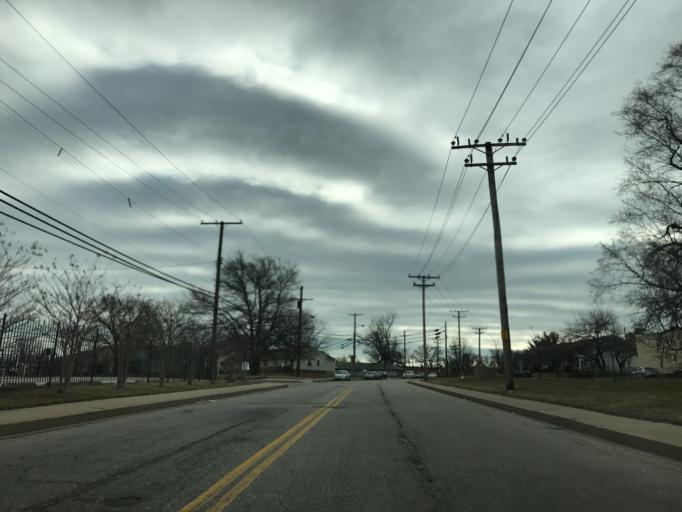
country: US
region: Maryland
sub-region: Baltimore County
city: Lansdowne
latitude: 39.2640
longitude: -76.6431
